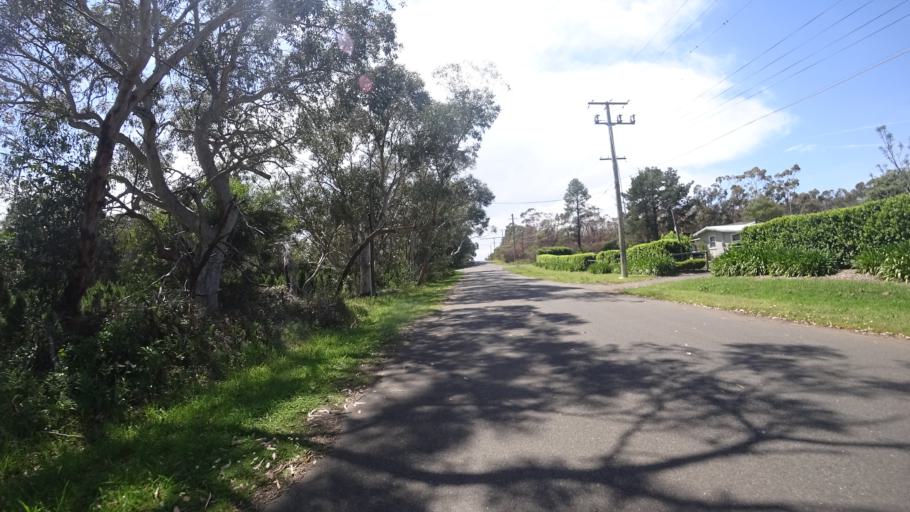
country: AU
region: New South Wales
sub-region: City of Sydney
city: North Turramurra
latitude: -33.6767
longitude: 151.1837
